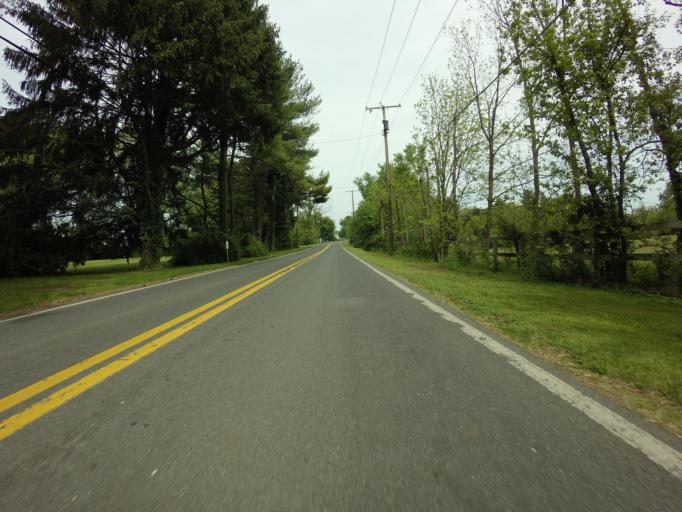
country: US
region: Maryland
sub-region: Baltimore County
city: Reisterstown
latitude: 39.4905
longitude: -76.8873
